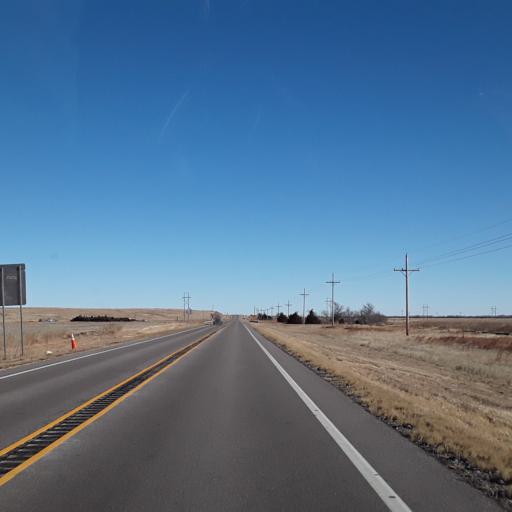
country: US
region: Kansas
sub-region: Pawnee County
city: Larned
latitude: 38.0839
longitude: -99.2312
